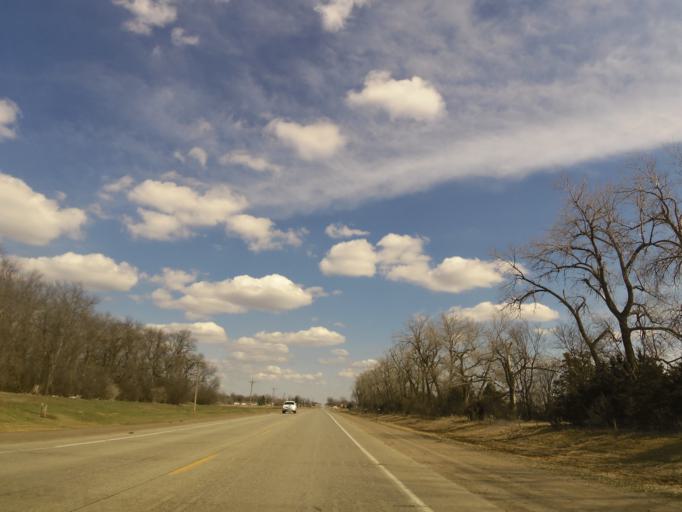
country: US
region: South Dakota
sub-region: Codington County
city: Watertown
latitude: 44.8901
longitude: -96.9343
